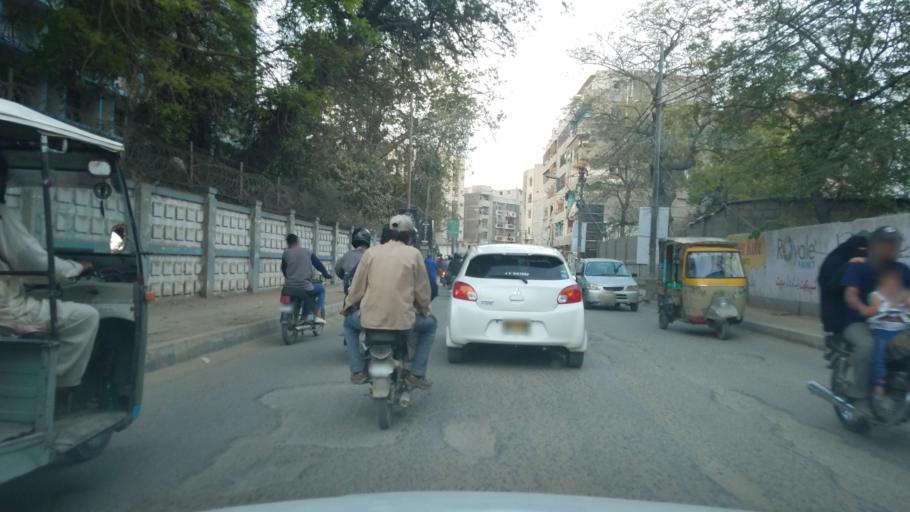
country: PK
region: Sindh
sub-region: Karachi District
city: Karachi
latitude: 24.8726
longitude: 67.0287
